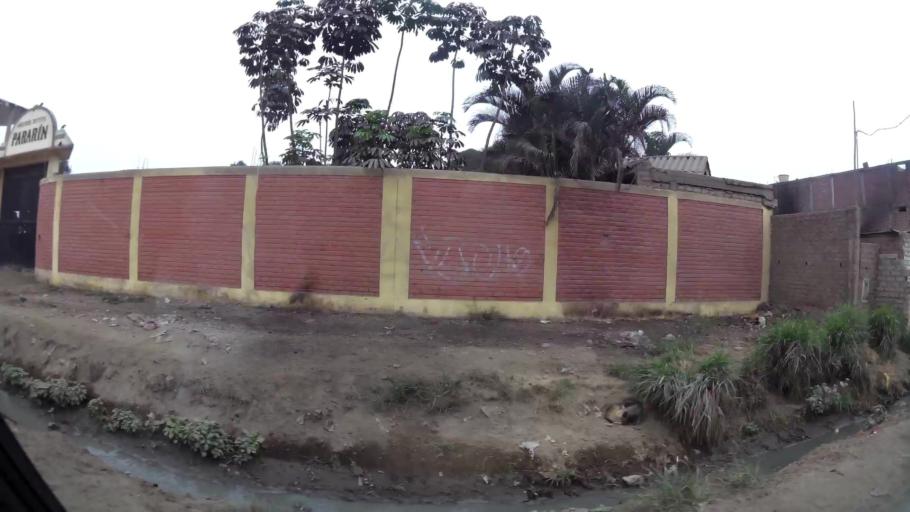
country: PE
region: Lima
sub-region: Lima
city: Urb. Santo Domingo
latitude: -11.8932
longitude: -77.0617
